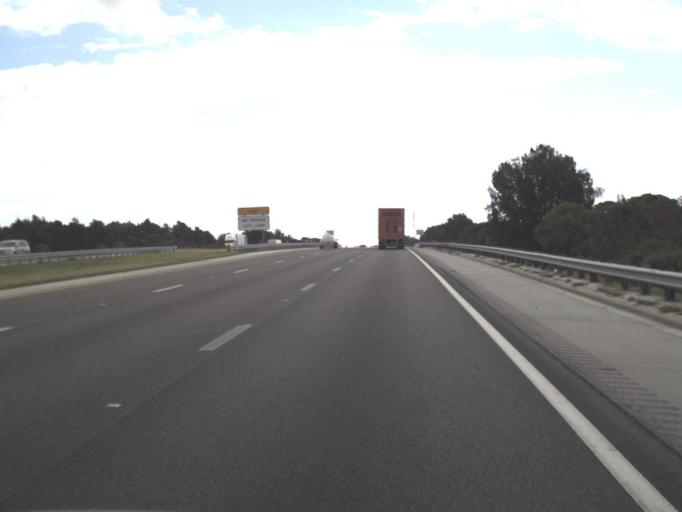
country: US
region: Florida
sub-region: Sarasota County
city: Plantation
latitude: 27.1091
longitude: -82.3702
